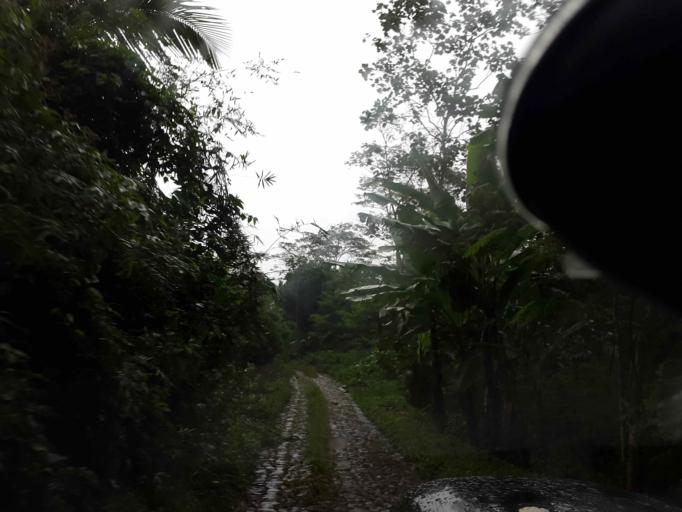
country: ID
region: Central Java
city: Wonosobo
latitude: -7.4694
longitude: 110.0109
